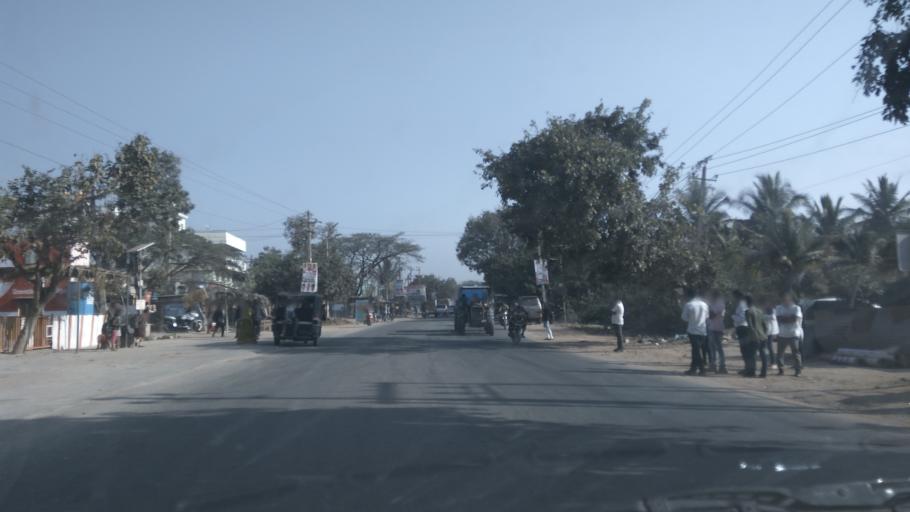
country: IN
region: Karnataka
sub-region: Bangalore Rural
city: Hoskote
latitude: 13.0788
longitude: 77.7369
